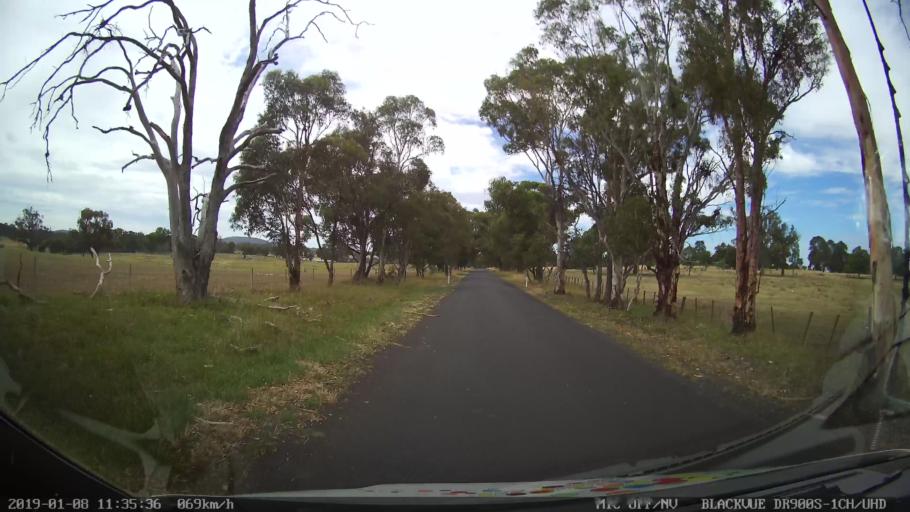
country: AU
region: New South Wales
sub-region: Guyra
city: Guyra
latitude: -30.3388
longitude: 151.5382
